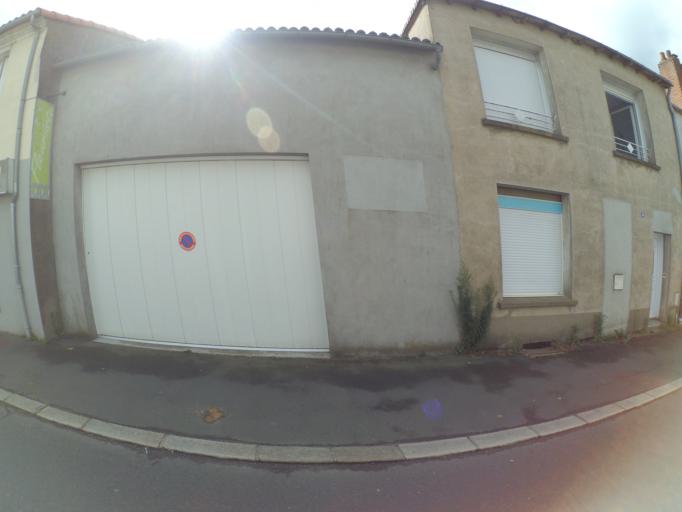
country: FR
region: Pays de la Loire
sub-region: Departement de Maine-et-Loire
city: Villedieu-la-Blouere
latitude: 47.1472
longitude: -1.0635
